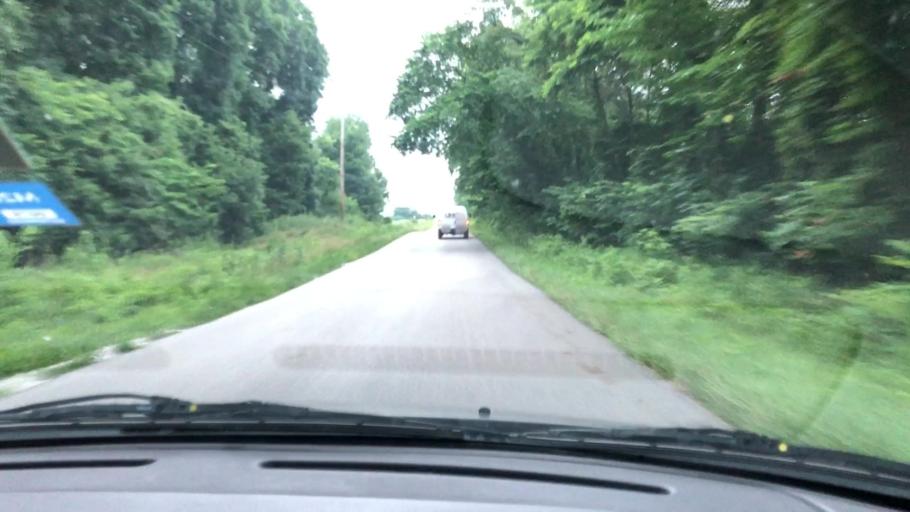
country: US
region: Indiana
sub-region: Greene County
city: Linton
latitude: 38.9767
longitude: -87.3047
